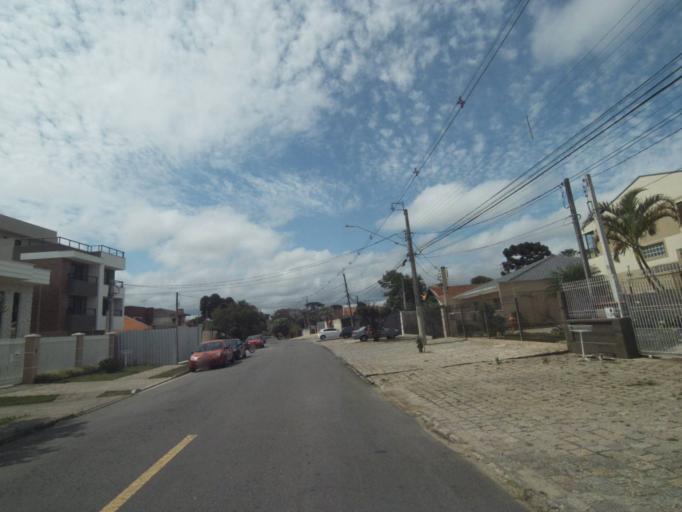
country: BR
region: Parana
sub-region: Pinhais
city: Pinhais
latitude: -25.4361
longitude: -49.2318
